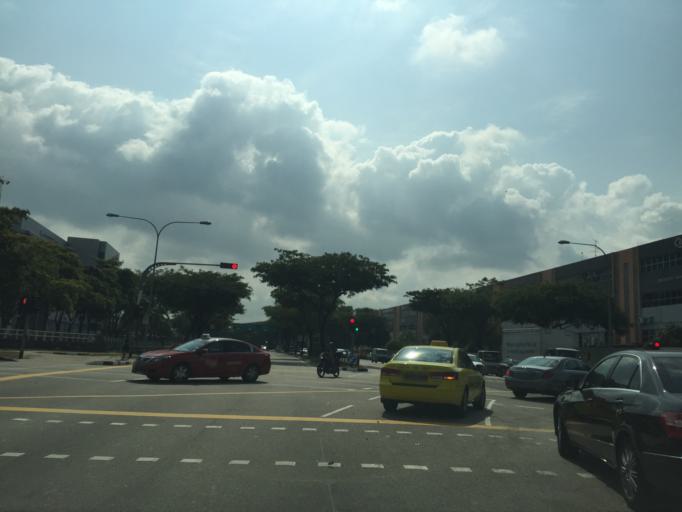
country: SG
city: Singapore
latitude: 1.3357
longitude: 103.8937
